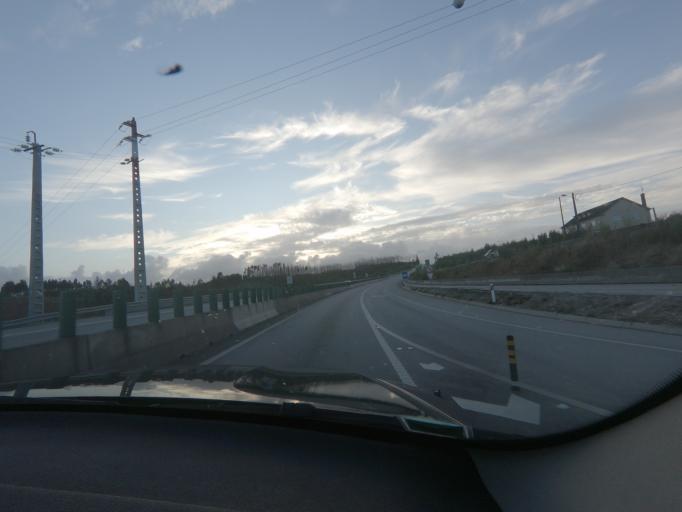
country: PT
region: Viseu
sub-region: Mortagua
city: Mortagua
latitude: 40.3487
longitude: -8.1857
